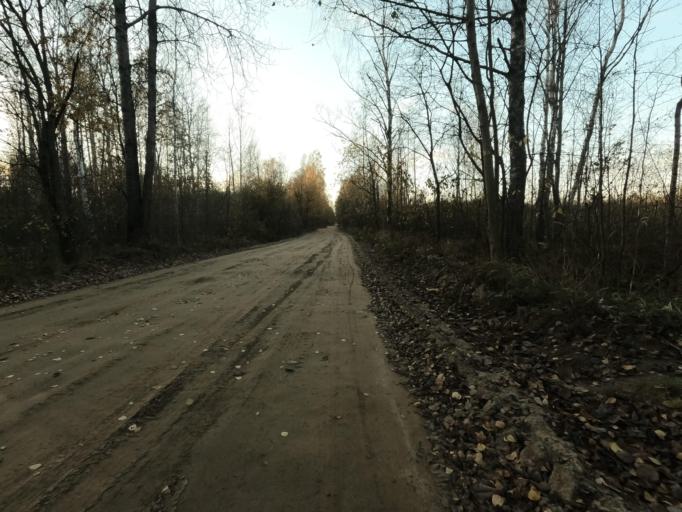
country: RU
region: Leningrad
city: Mga
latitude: 59.7583
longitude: 31.2688
